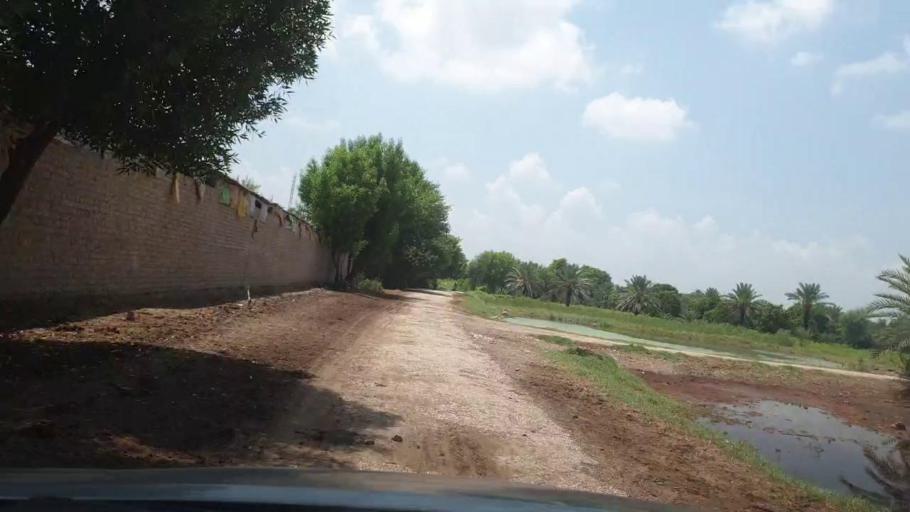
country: PK
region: Sindh
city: Pir jo Goth
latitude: 27.6097
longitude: 68.6104
